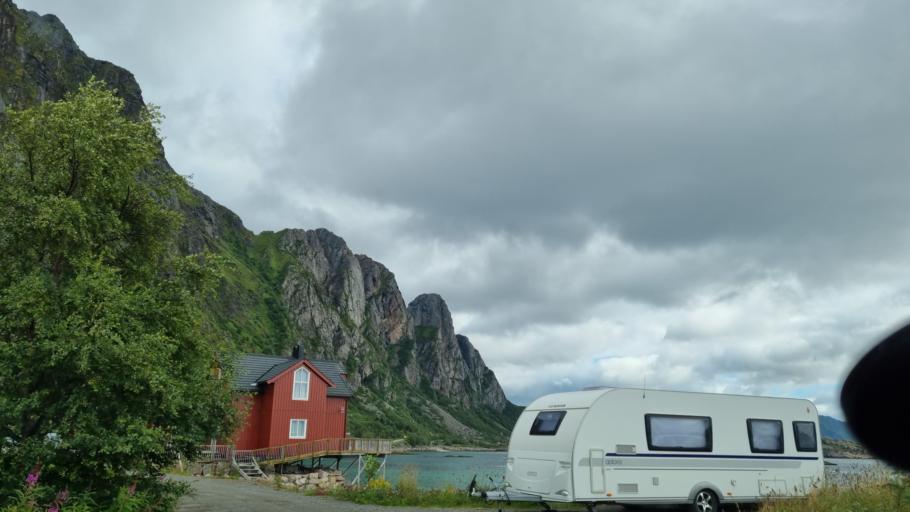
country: NO
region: Nordland
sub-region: Vagan
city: Svolvaer
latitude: 68.2401
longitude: 14.5896
